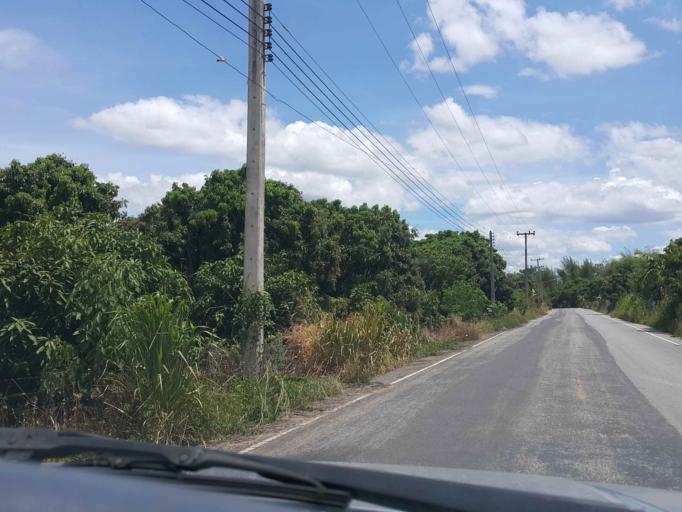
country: TH
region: Chiang Mai
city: Doi Lo
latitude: 18.5275
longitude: 98.7762
